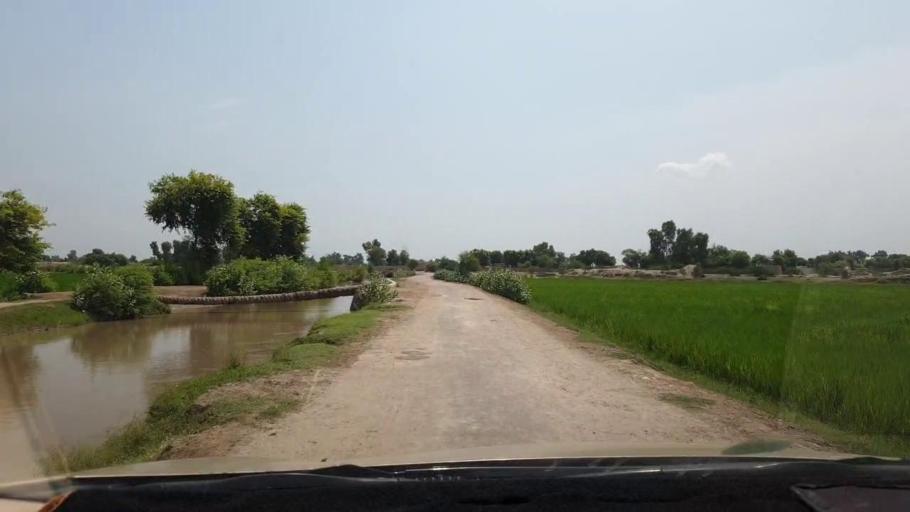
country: PK
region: Sindh
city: Naudero
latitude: 27.6583
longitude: 68.3304
